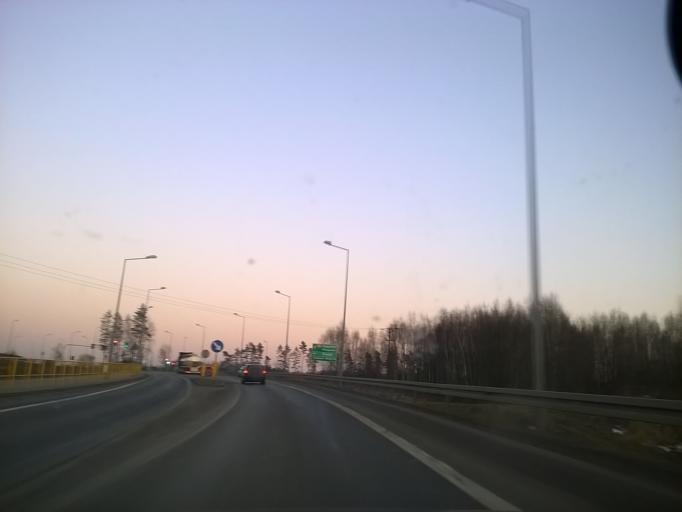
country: PL
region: Warmian-Masurian Voivodeship
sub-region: Powiat olsztynski
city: Olsztyn
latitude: 53.7782
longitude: 20.5604
